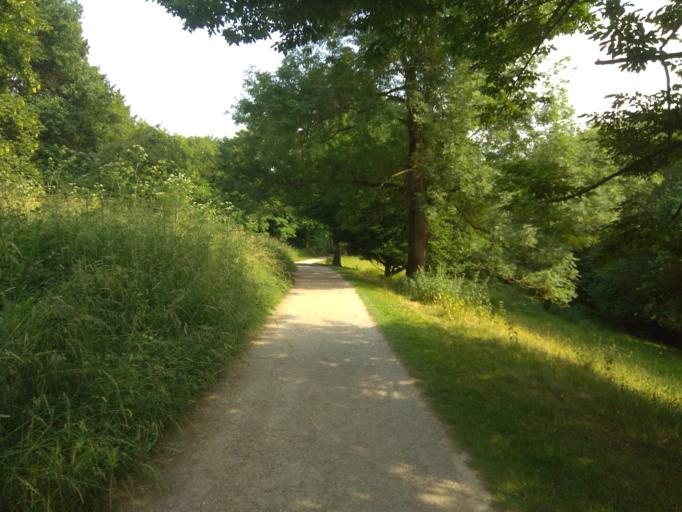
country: DE
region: Hesse
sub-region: Regierungsbezirk Kassel
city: Kassel
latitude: 51.3333
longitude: 9.5246
